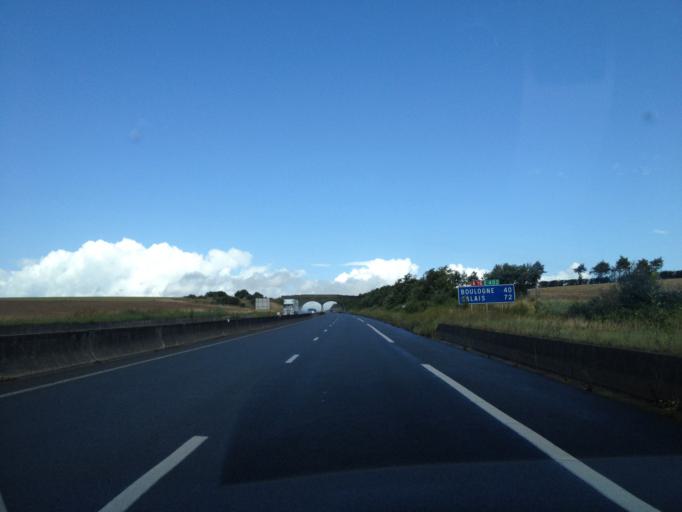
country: FR
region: Nord-Pas-de-Calais
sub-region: Departement du Pas-de-Calais
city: Verton
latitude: 50.4186
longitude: 1.6943
